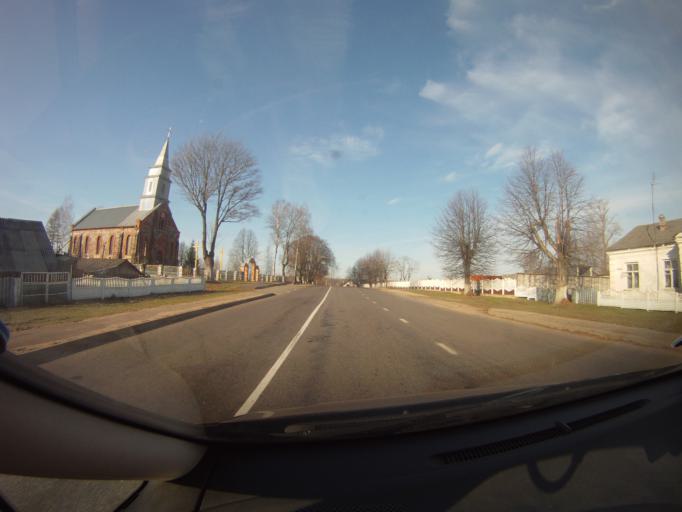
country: BY
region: Minsk
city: Il'ya
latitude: 54.4124
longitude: 27.2904
